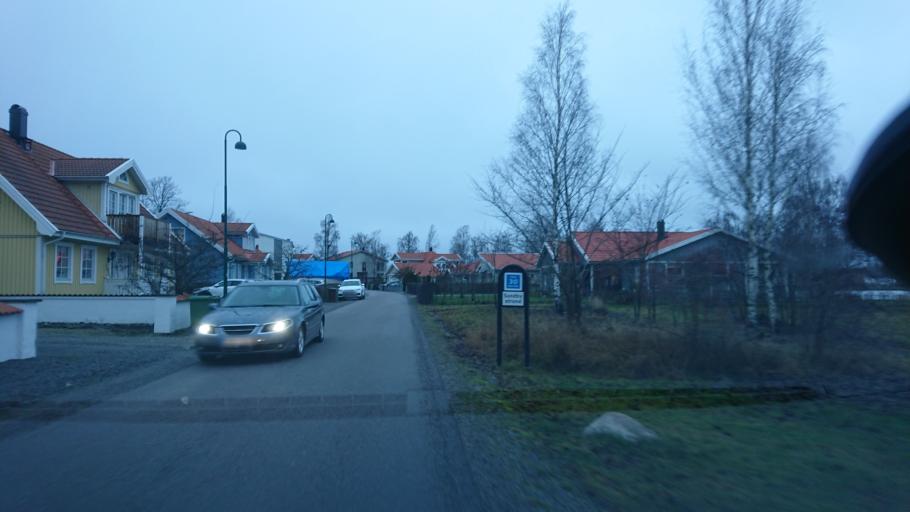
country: SE
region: Soedermanland
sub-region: Strangnas Kommun
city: Stallarholmen
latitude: 59.3626
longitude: 17.1987
